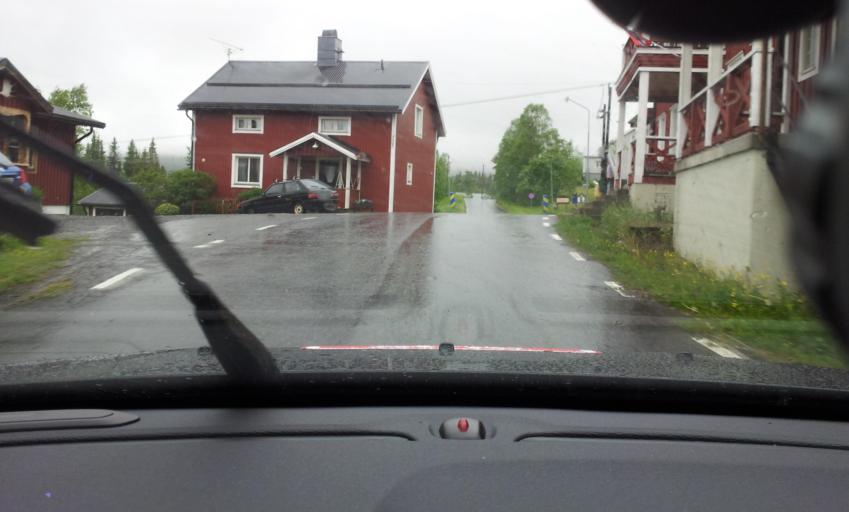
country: SE
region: Jaemtland
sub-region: Are Kommun
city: Are
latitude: 63.3150
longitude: 13.0676
